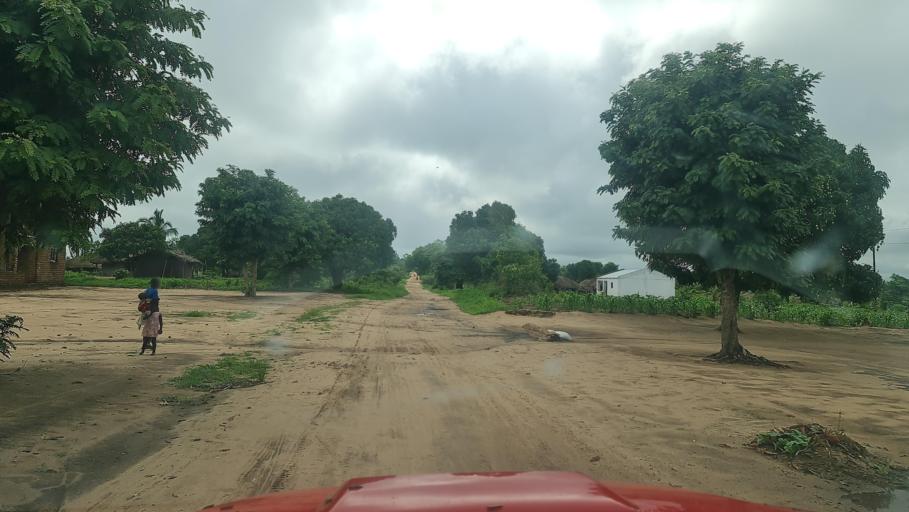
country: MW
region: Southern Region
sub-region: Nsanje District
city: Nsanje
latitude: -17.2030
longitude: 35.6913
